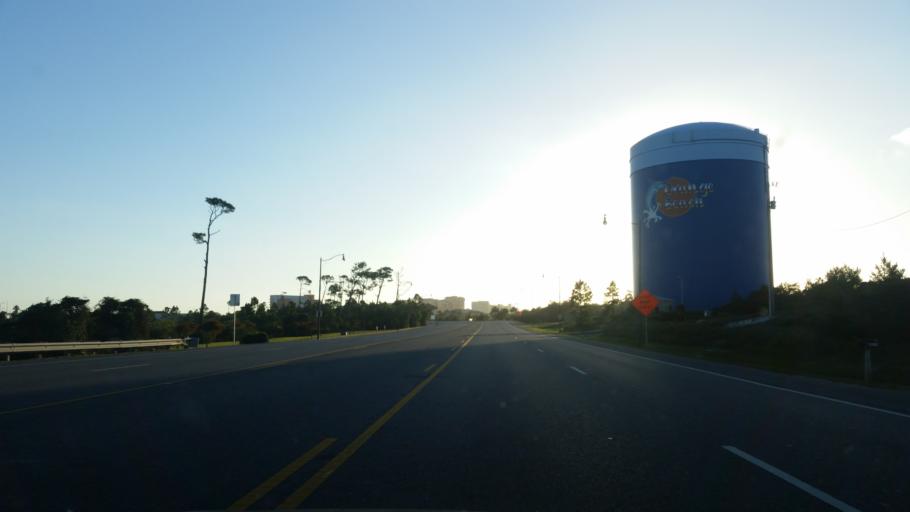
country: US
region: Alabama
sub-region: Baldwin County
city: Orange Beach
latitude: 30.2736
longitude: -87.5826
